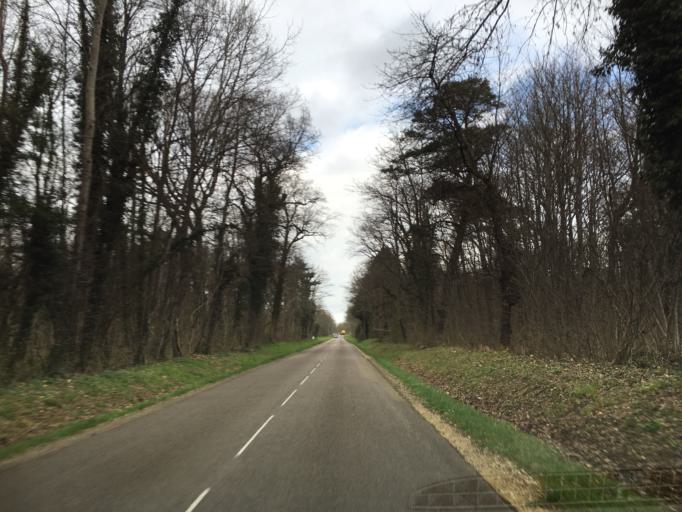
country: FR
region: Bourgogne
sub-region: Departement de l'Yonne
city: Charbuy
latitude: 47.8120
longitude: 3.4485
